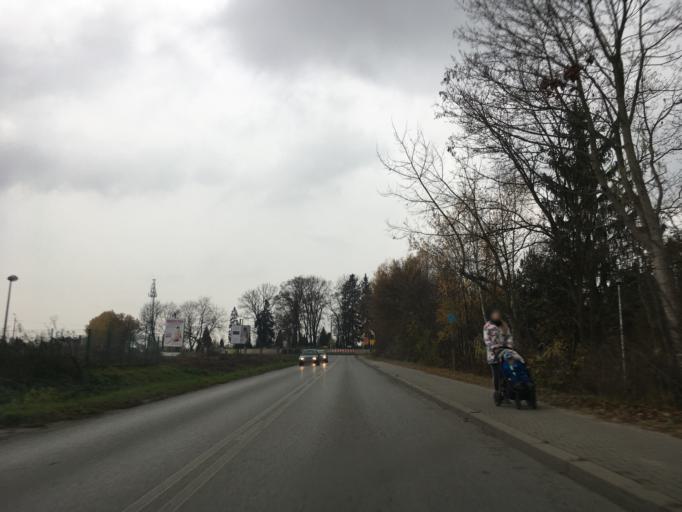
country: PL
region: Masovian Voivodeship
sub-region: Powiat piaseczynski
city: Zalesie Gorne
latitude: 52.0421
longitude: 21.0027
